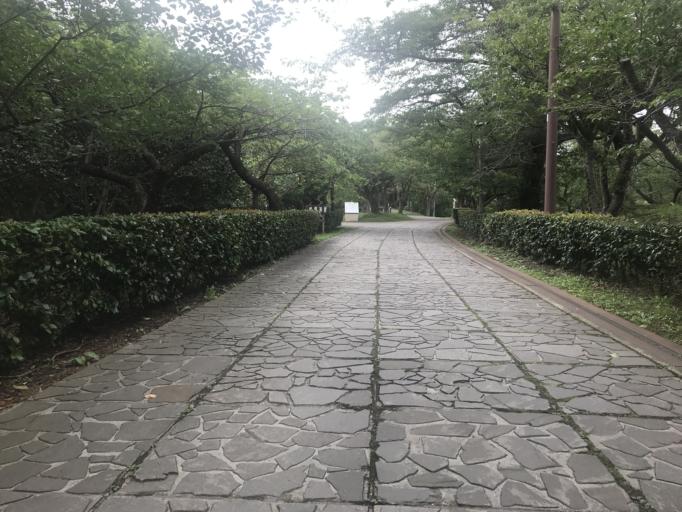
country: JP
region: Hokkaido
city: Kamiiso
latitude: 41.4320
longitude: 140.1089
